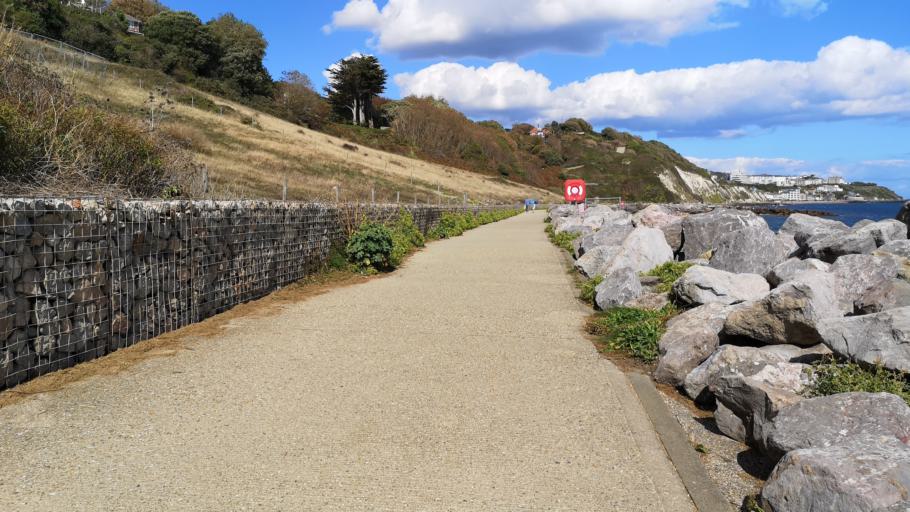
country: GB
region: England
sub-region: Isle of Wight
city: Ventnor
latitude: 50.5888
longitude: -1.2225
